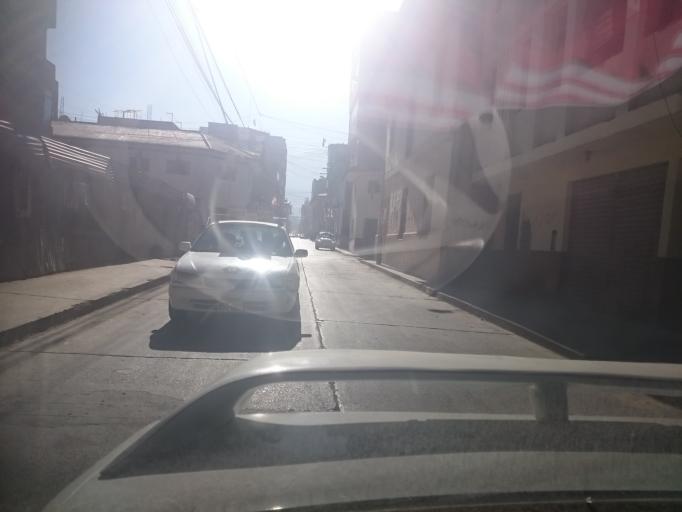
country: PE
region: Junin
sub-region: Provincia de Huancayo
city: Huancayo
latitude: -12.0740
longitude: -75.2085
